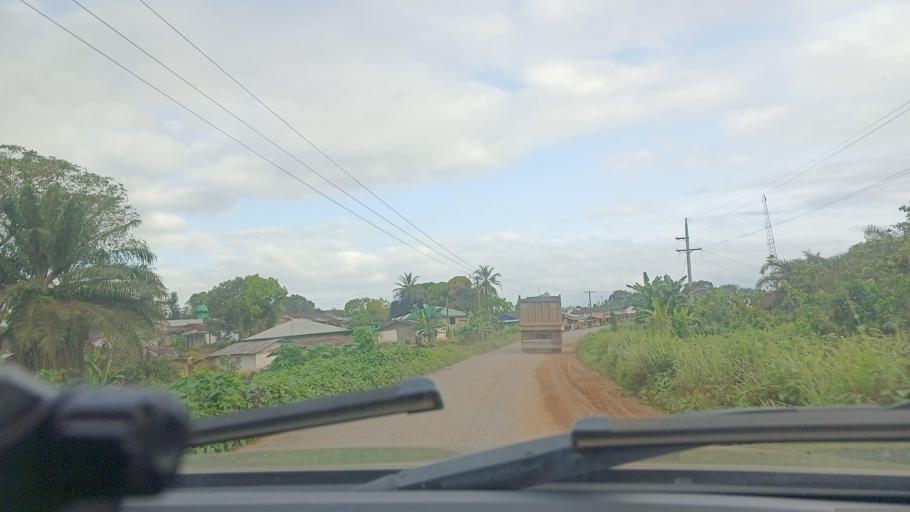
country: LR
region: Montserrado
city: Monrovia
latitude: 6.5809
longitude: -10.8898
